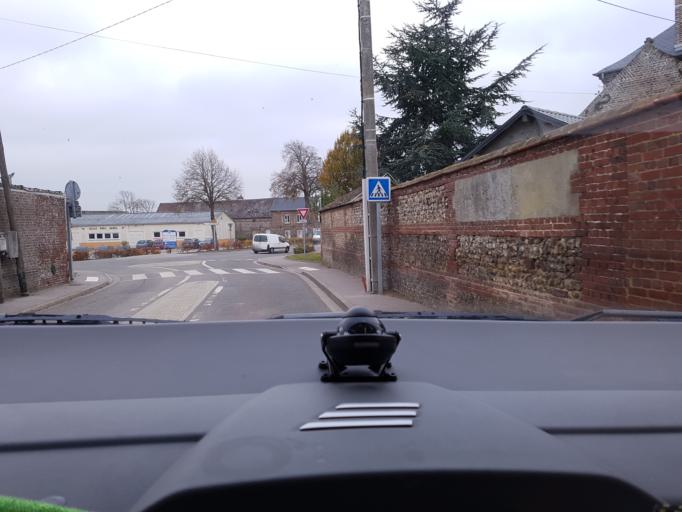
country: FR
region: Haute-Normandie
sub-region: Departement de la Seine-Maritime
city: Le Treport
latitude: 50.0381
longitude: 1.3637
